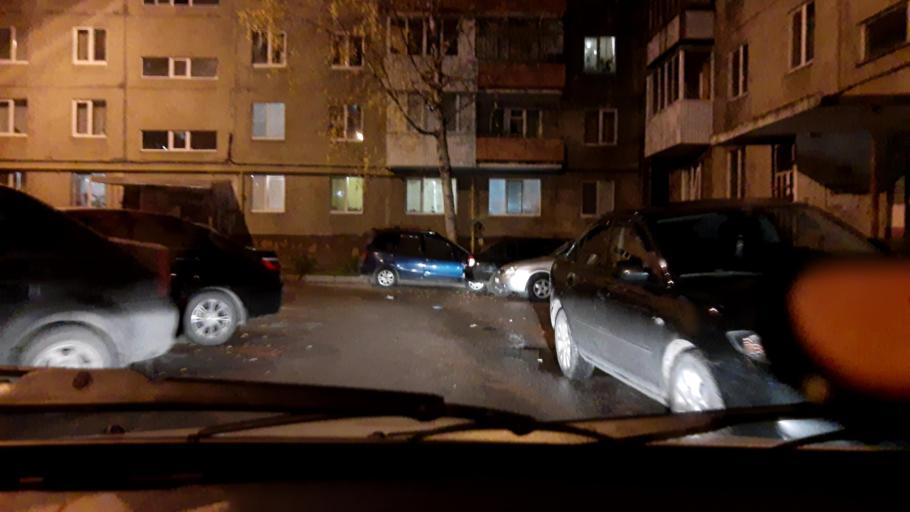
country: RU
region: Bashkortostan
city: Ufa
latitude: 54.8149
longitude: 56.1329
